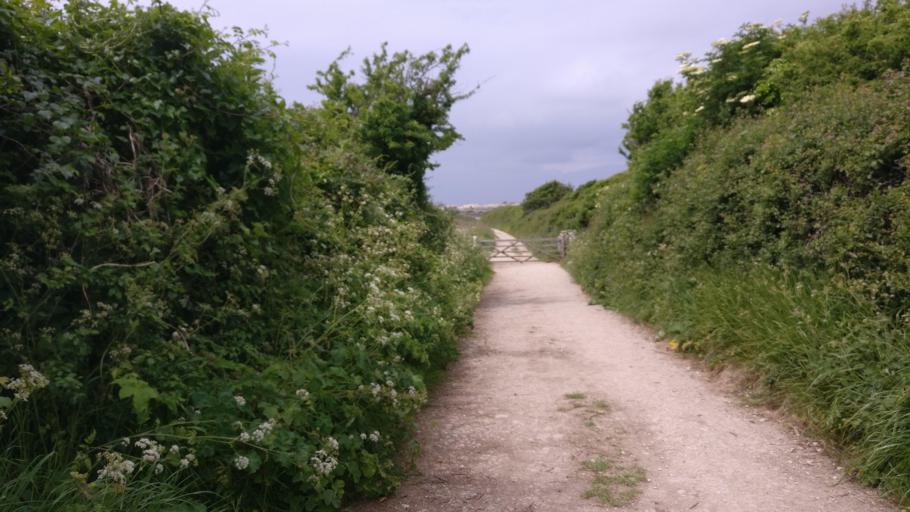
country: GB
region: England
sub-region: Dorset
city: Swanage
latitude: 50.6013
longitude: -2.0050
